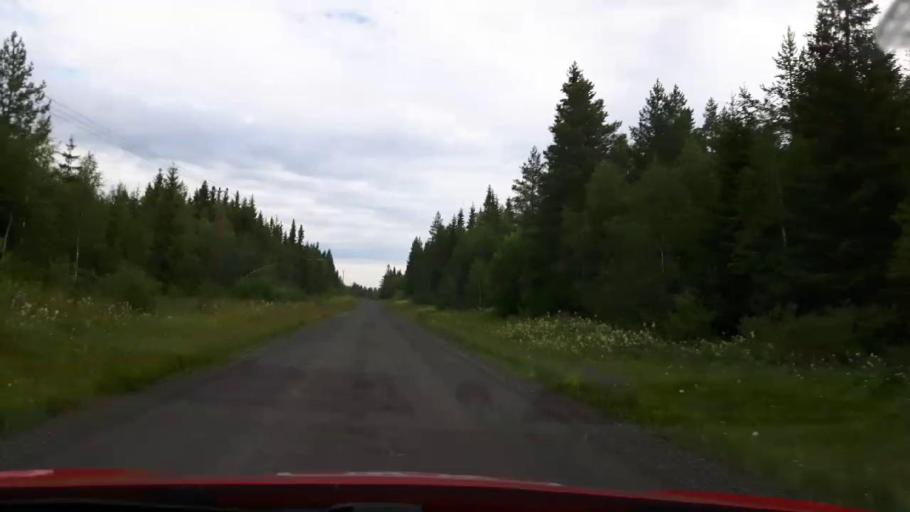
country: SE
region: Jaemtland
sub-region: Stroemsunds Kommun
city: Stroemsund
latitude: 63.5106
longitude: 15.3403
